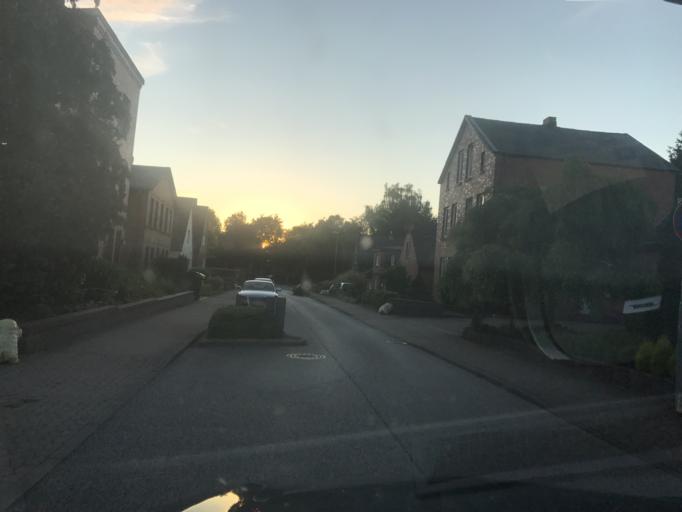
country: DE
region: Schleswig-Holstein
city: Itzehoe
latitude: 53.9293
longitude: 9.5013
